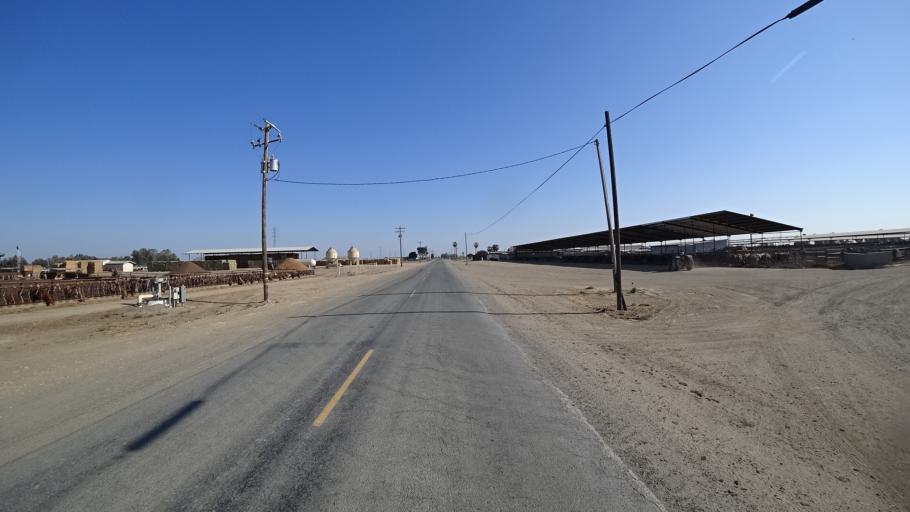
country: US
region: California
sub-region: Kings County
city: Lemoore Station
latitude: 36.3473
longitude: -119.8871
